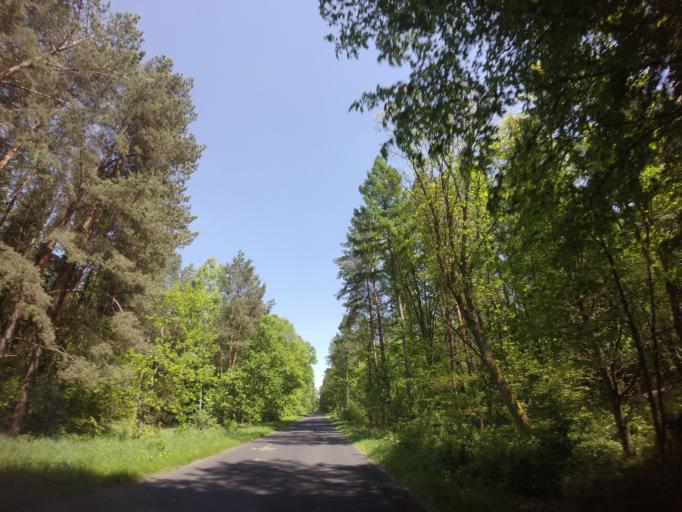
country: PL
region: West Pomeranian Voivodeship
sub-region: Powiat mysliborski
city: Barlinek
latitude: 52.9297
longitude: 15.1674
